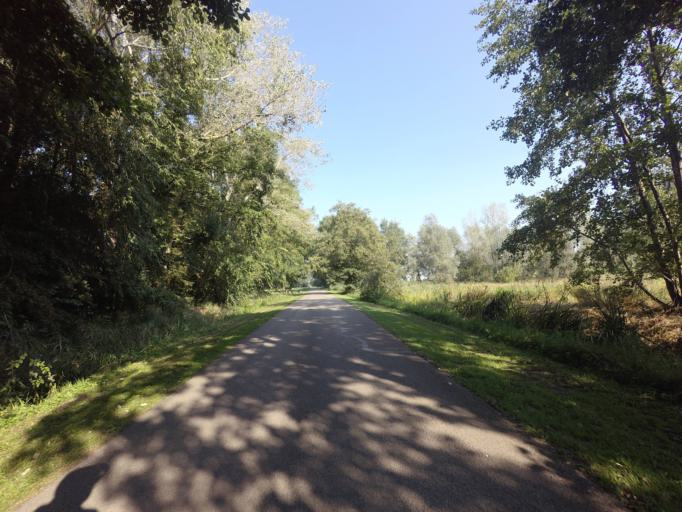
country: NL
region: Groningen
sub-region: Gemeente Zuidhorn
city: Aduard
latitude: 53.1945
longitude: 6.4505
